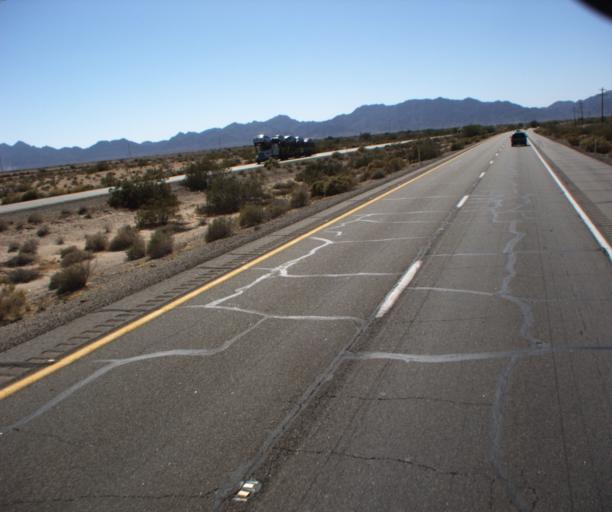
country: US
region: Arizona
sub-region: Yuma County
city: Wellton
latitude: 32.6504
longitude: -114.1915
